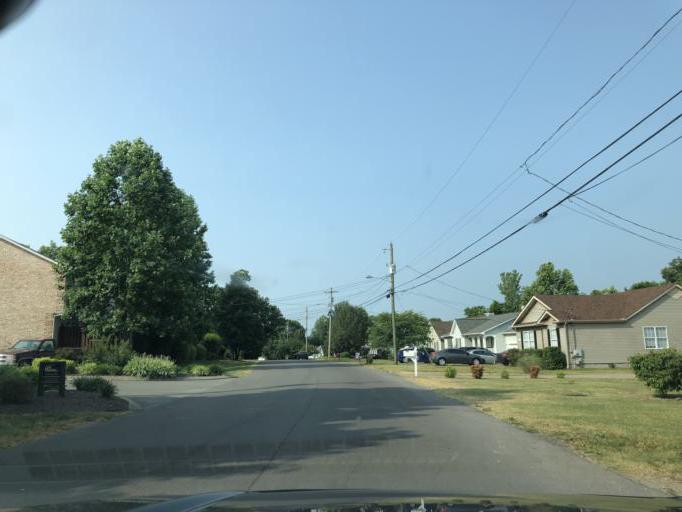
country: US
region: Tennessee
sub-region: Rutherford County
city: La Vergne
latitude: 36.0478
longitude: -86.6393
